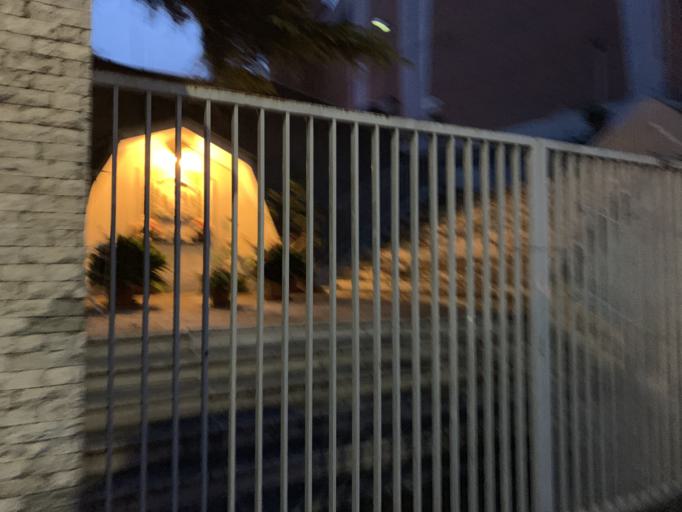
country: VA
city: Vatican City
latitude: 41.8832
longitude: 12.4191
